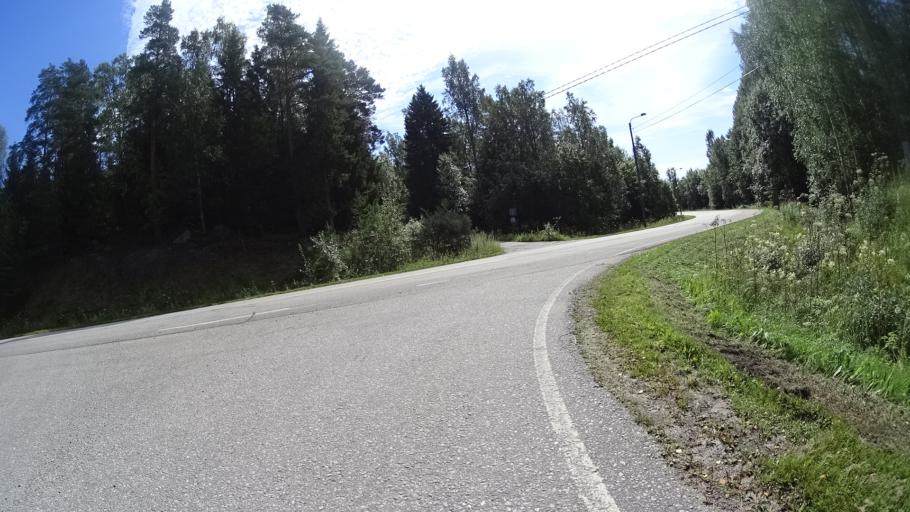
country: FI
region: Uusimaa
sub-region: Helsinki
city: Kirkkonummi
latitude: 60.1063
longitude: 24.4791
